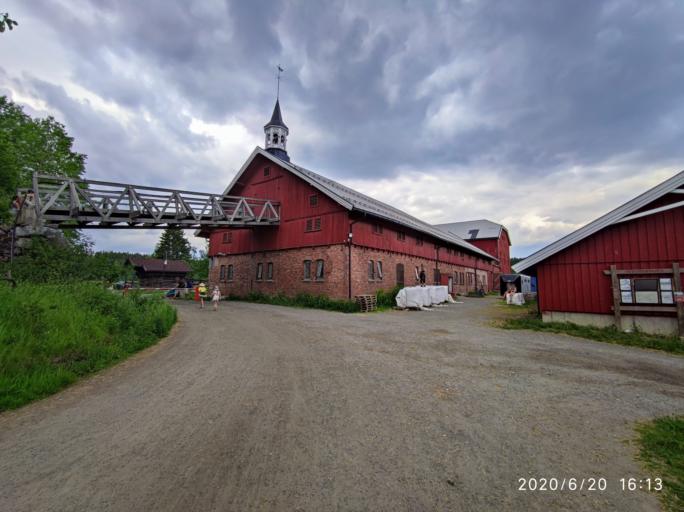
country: NO
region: Akershus
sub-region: Lorenskog
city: Kjenn
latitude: 59.8900
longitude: 10.9839
